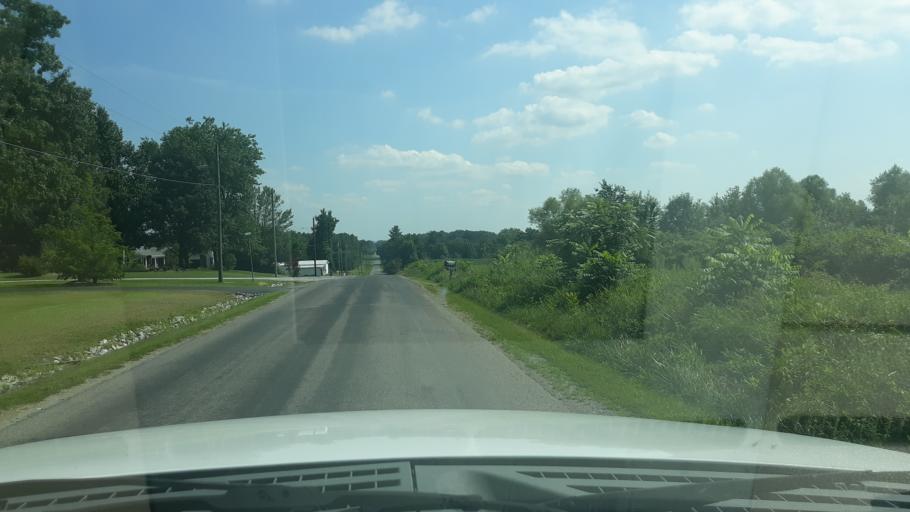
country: US
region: Illinois
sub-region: Saline County
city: Eldorado
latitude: 37.8261
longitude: -88.5025
